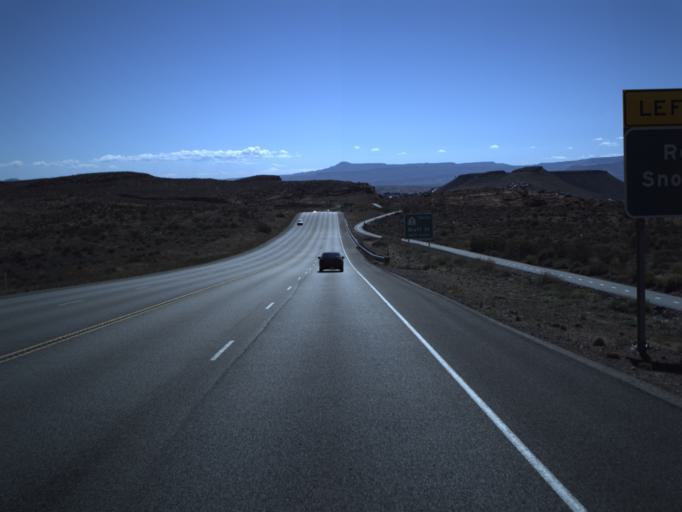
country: US
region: Utah
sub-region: Washington County
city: Saint George
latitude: 37.1448
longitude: -113.6062
